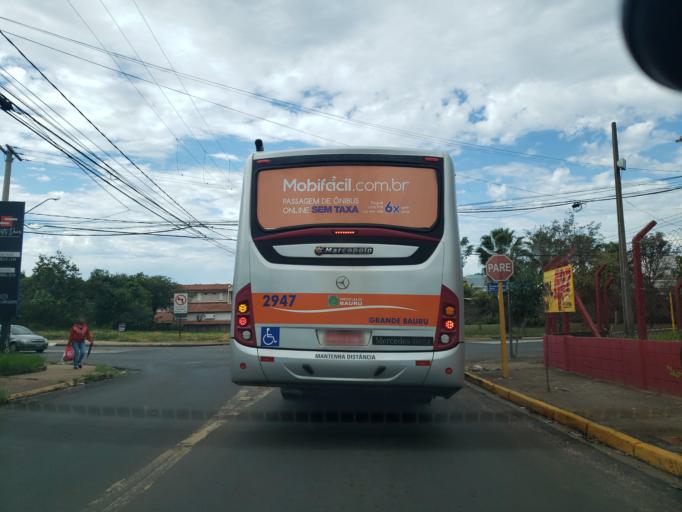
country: BR
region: Sao Paulo
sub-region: Bauru
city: Bauru
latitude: -22.3430
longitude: -49.0441
